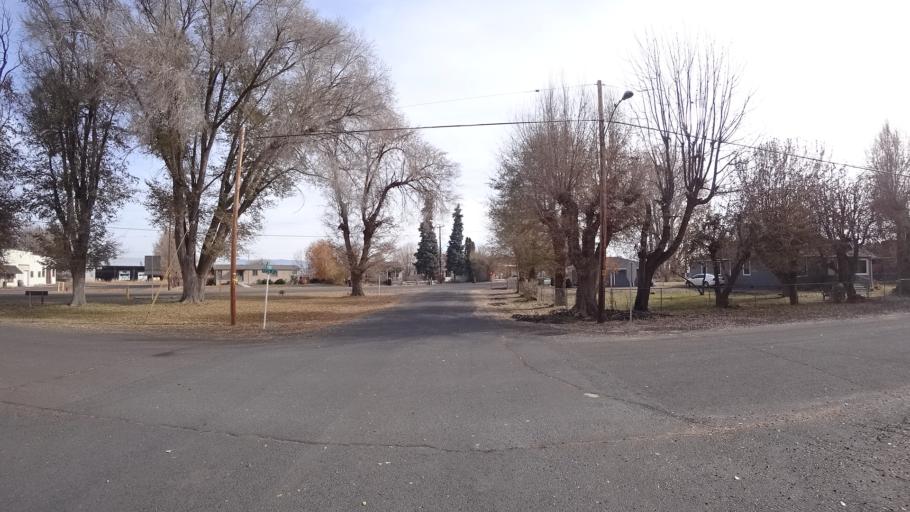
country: US
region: California
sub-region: Siskiyou County
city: Tulelake
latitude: 41.9548
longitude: -121.4740
